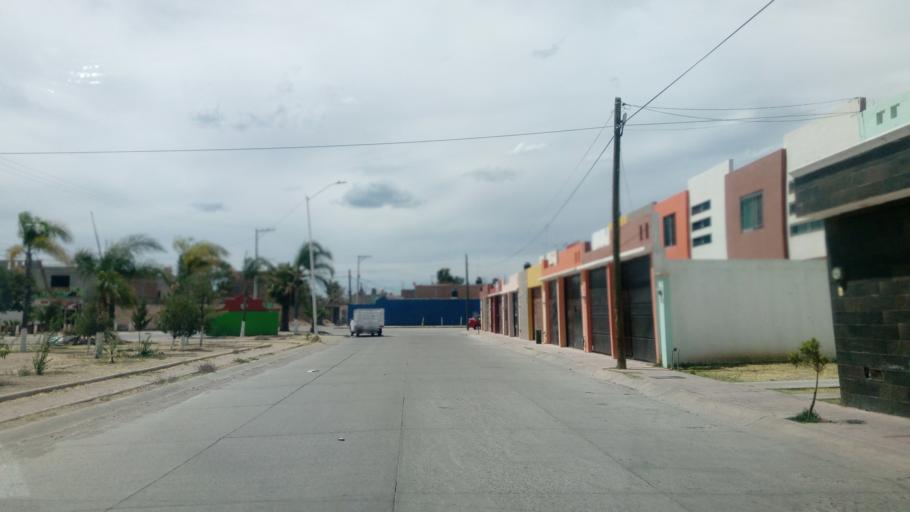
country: MX
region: Durango
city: Victoria de Durango
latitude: 23.9914
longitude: -104.6452
